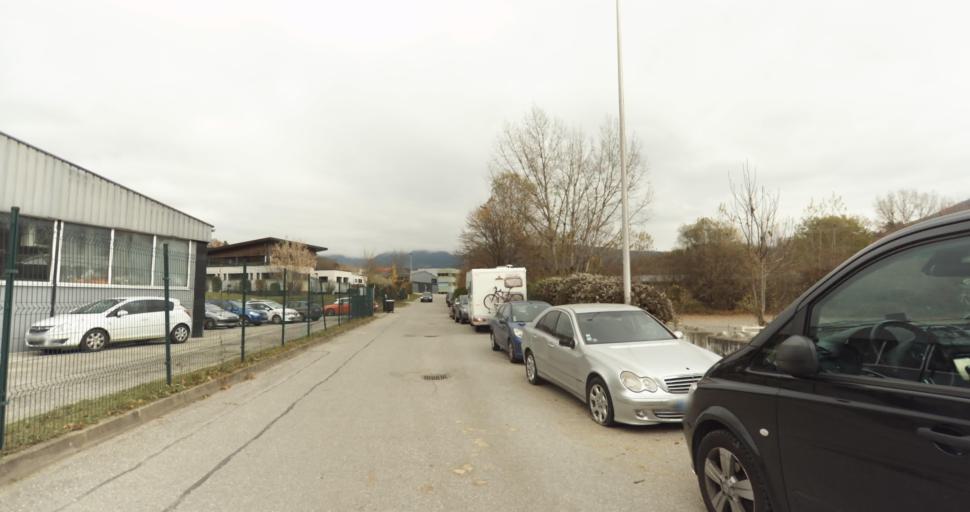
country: FR
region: Rhone-Alpes
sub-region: Departement de la Haute-Savoie
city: Pringy
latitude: 45.9364
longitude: 6.1371
